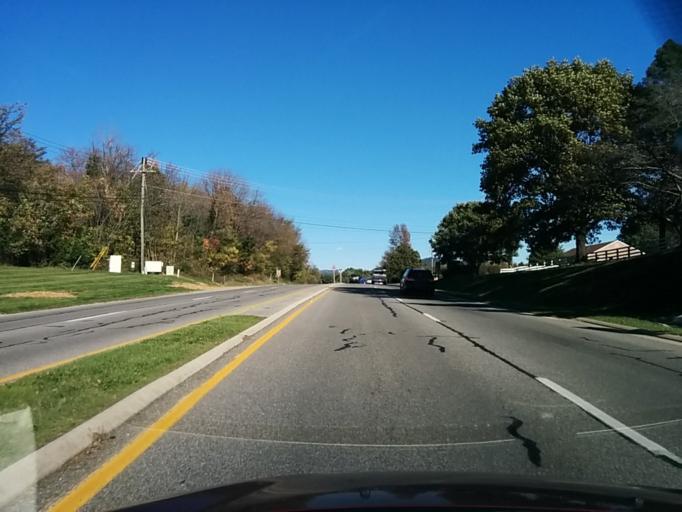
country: US
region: Virginia
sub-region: Roanoke County
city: Hollins
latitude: 37.3536
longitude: -79.9351
